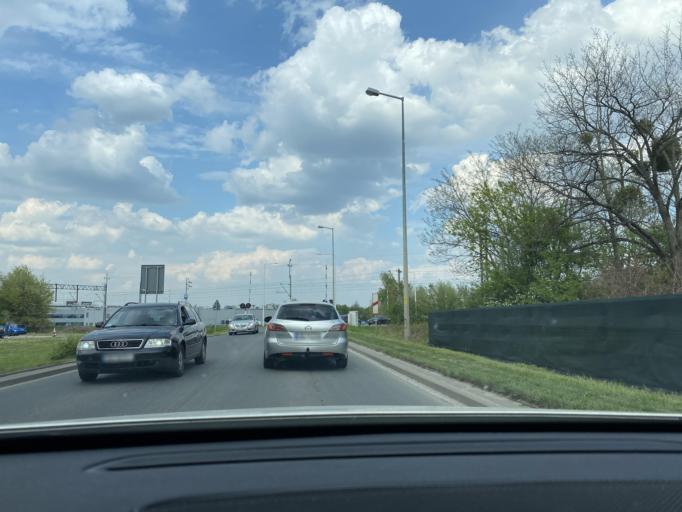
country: PL
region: Lower Silesian Voivodeship
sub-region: Powiat wroclawski
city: Wilczyce
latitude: 51.1199
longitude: 17.1159
